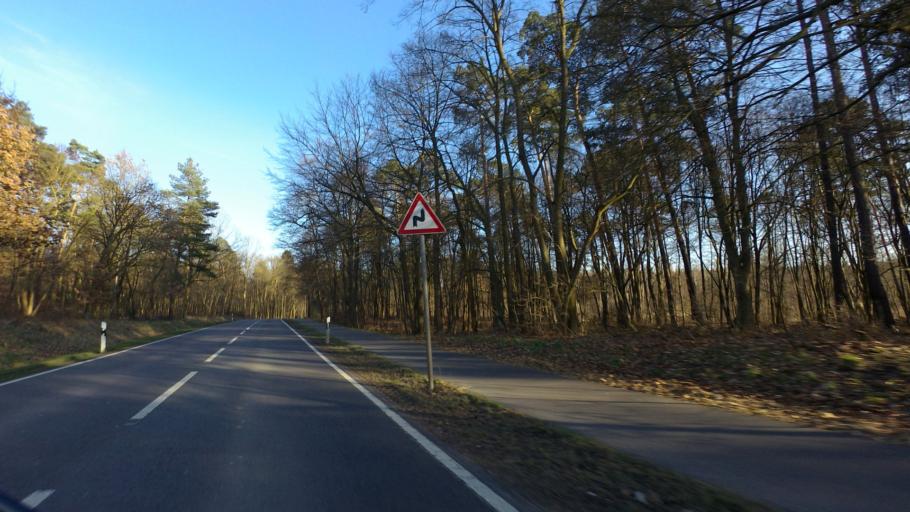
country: DE
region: Brandenburg
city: Britz
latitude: 52.8657
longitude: 13.8255
